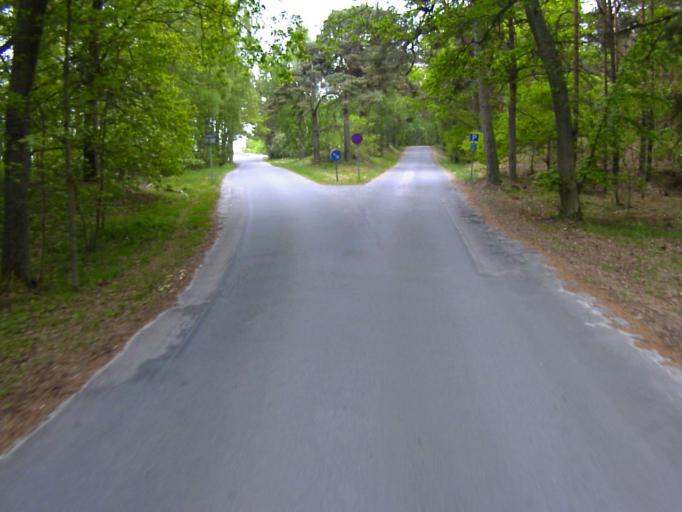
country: SE
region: Skane
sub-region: Kristianstads Kommun
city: Ahus
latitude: 55.9182
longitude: 14.3191
